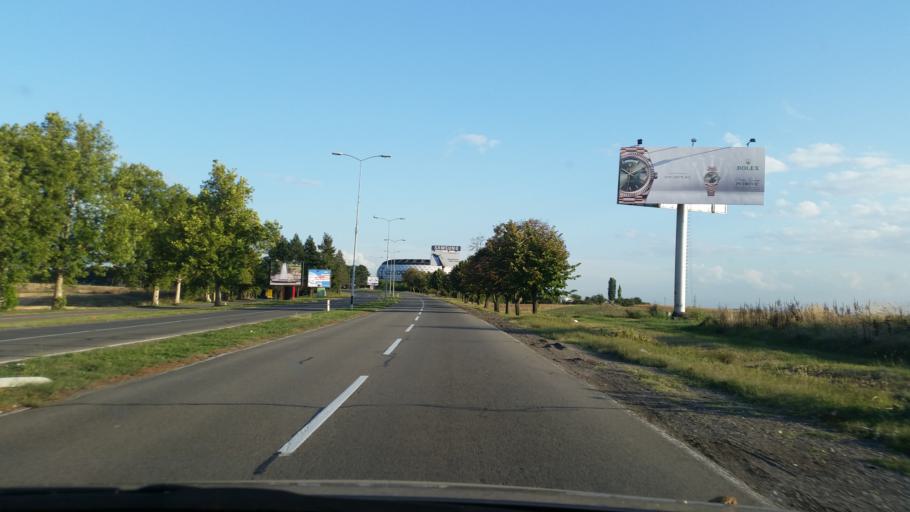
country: RS
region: Central Serbia
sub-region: Belgrade
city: Surcin
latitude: 44.8231
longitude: 20.2821
